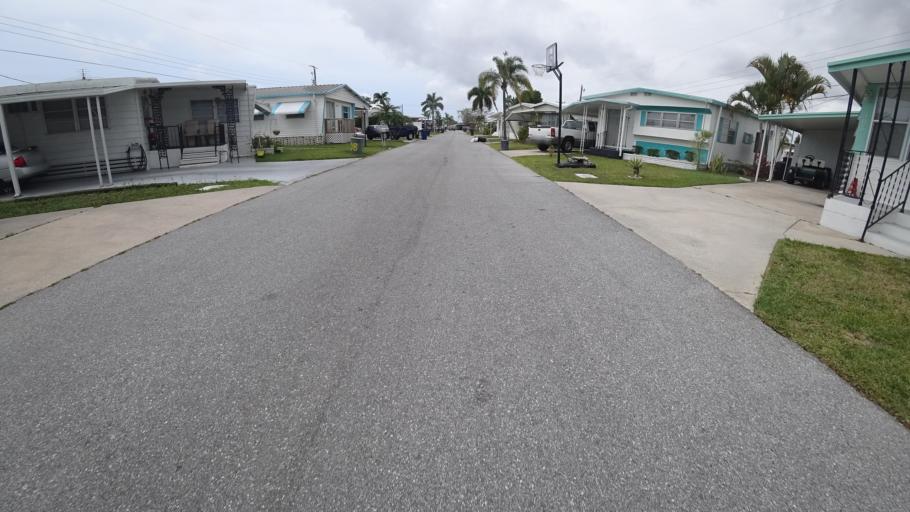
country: US
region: Florida
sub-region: Manatee County
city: South Bradenton
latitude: 27.4492
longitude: -82.5655
